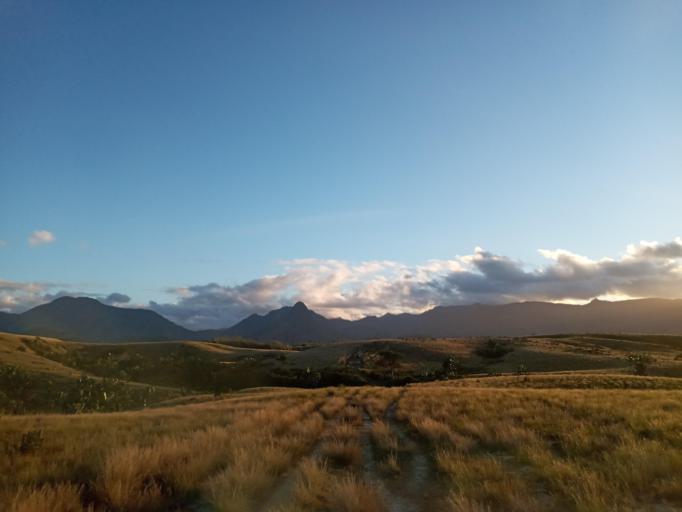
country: MG
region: Anosy
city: Fort Dauphin
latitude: -24.5146
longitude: 47.2475
